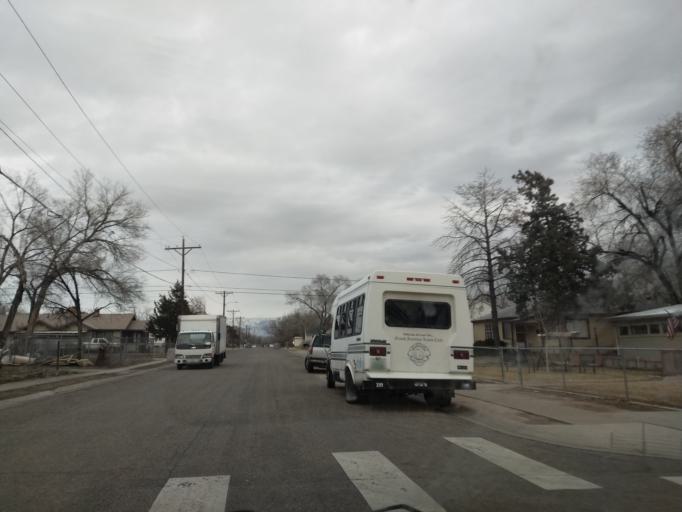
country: US
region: Colorado
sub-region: Mesa County
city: Grand Junction
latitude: 39.0723
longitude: -108.5477
